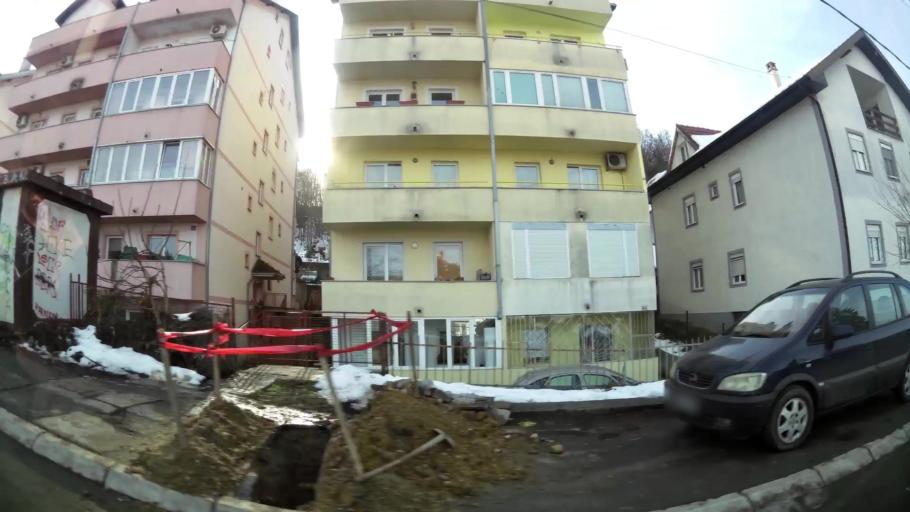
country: RS
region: Central Serbia
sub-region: Belgrade
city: Rakovica
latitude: 44.7291
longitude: 20.4281
